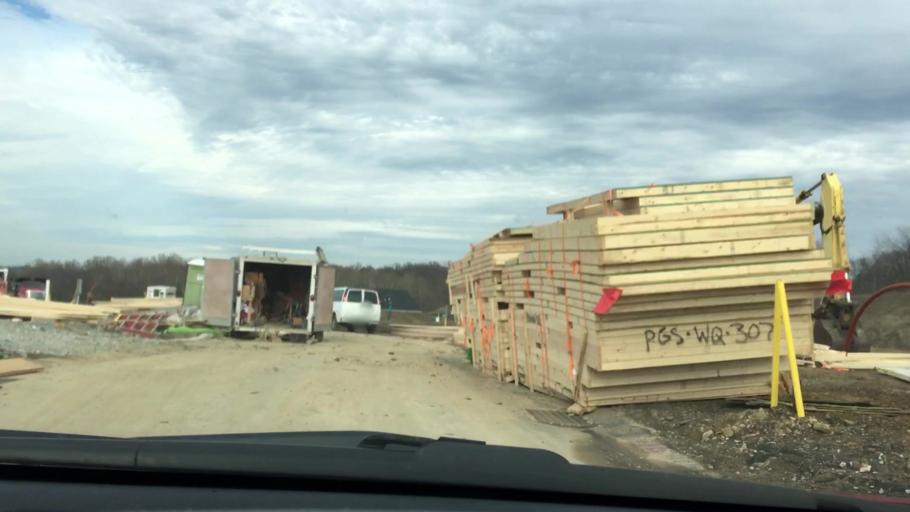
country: US
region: Pennsylvania
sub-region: Allegheny County
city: South Park Township
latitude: 40.2976
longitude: -79.9687
